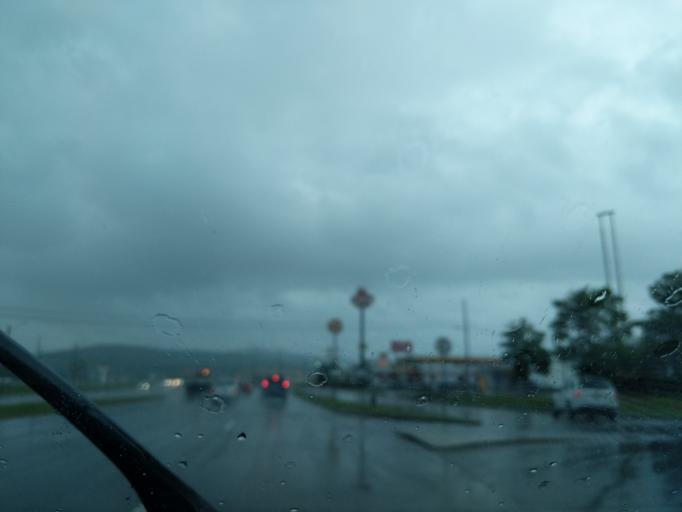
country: US
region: Alabama
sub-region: Calhoun County
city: Oxford
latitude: 33.6073
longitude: -85.8287
